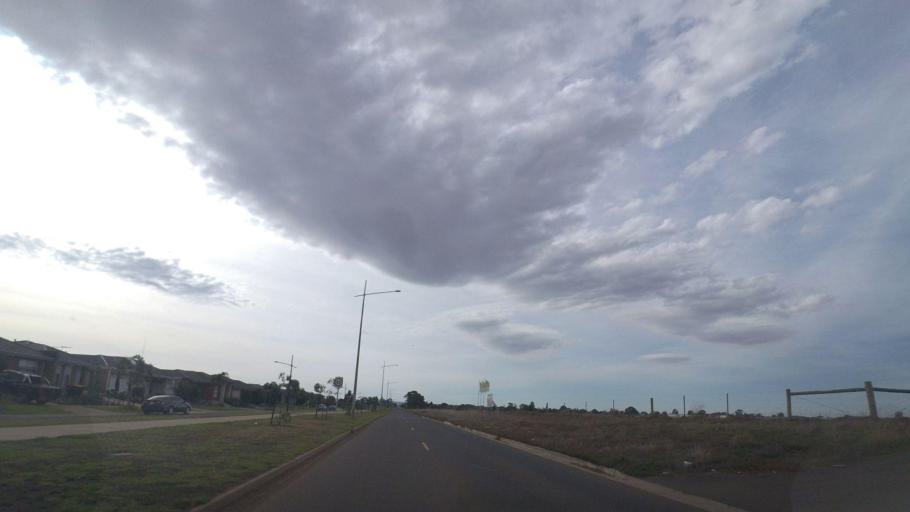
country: AU
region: Victoria
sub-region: Melton
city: Melton South
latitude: -37.7183
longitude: 144.5618
